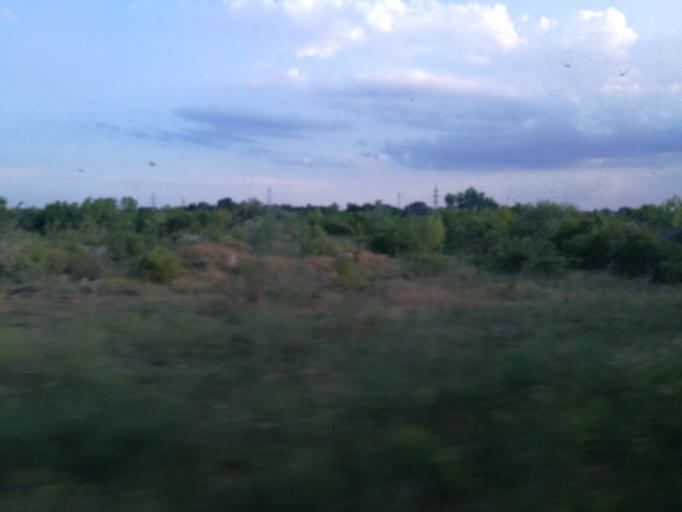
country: RO
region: Dambovita
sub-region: Comuna Titu
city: Salcuta
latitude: 44.6614
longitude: 25.5830
